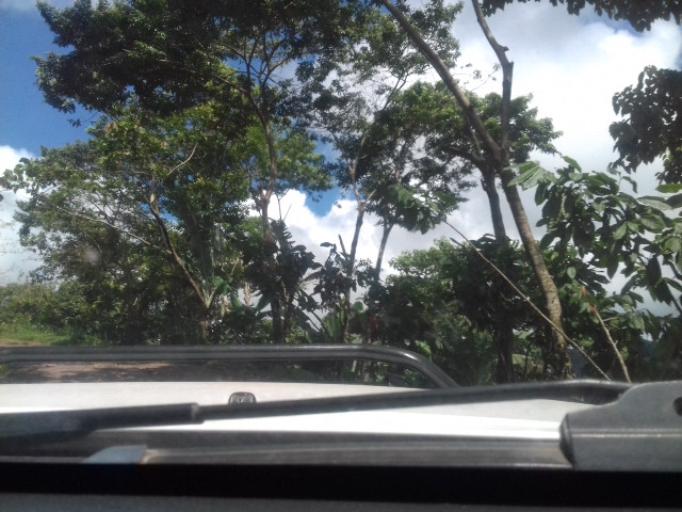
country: NI
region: Atlantico Norte (RAAN)
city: Waslala
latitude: 13.2243
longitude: -85.5714
